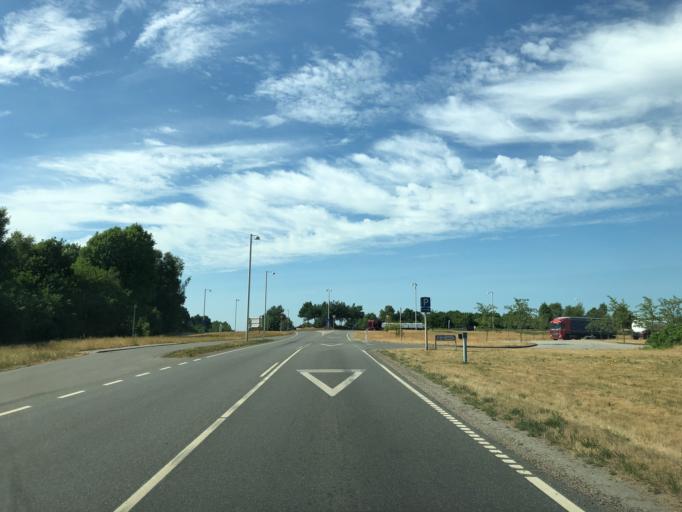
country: DK
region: Central Jutland
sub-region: Ikast-Brande Kommune
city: Brande
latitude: 55.9642
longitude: 9.0978
